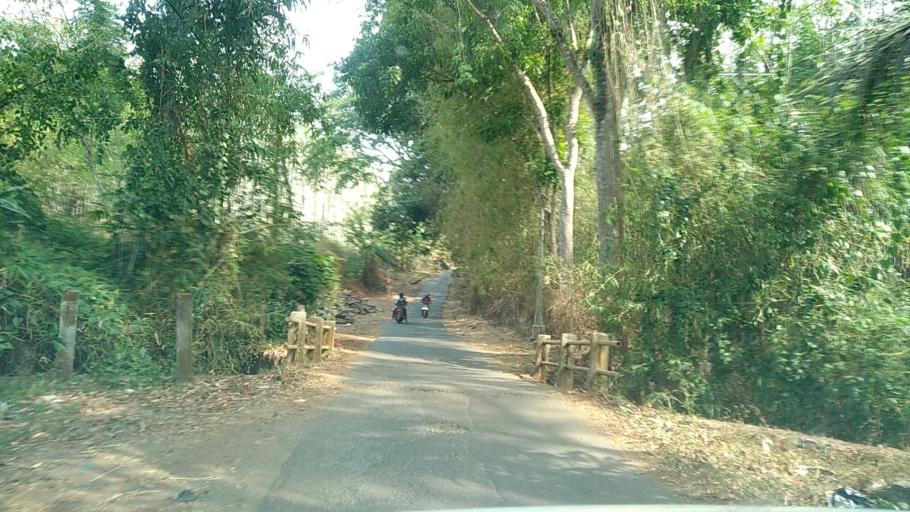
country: ID
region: Central Java
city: Semarang
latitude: -7.0230
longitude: 110.3108
